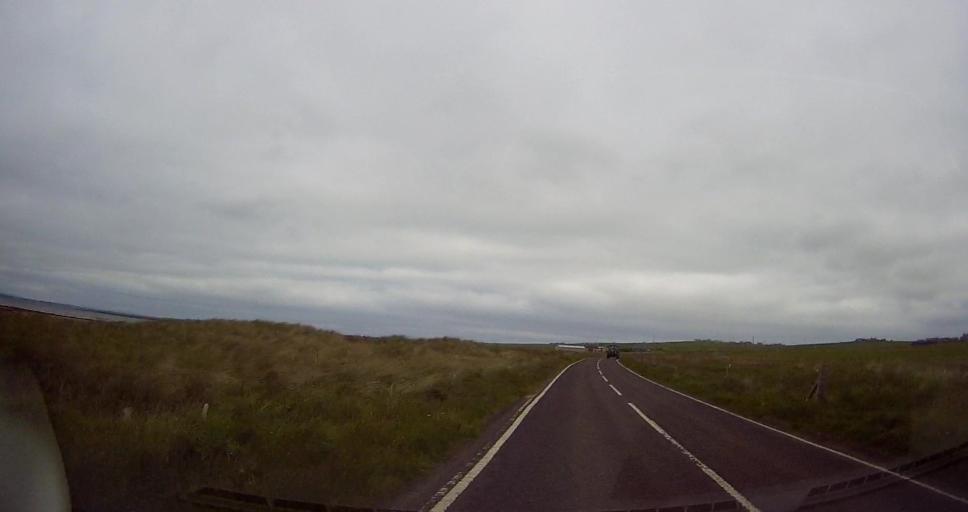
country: GB
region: Scotland
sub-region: Orkney Islands
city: Kirkwall
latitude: 58.9175
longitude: -2.7815
